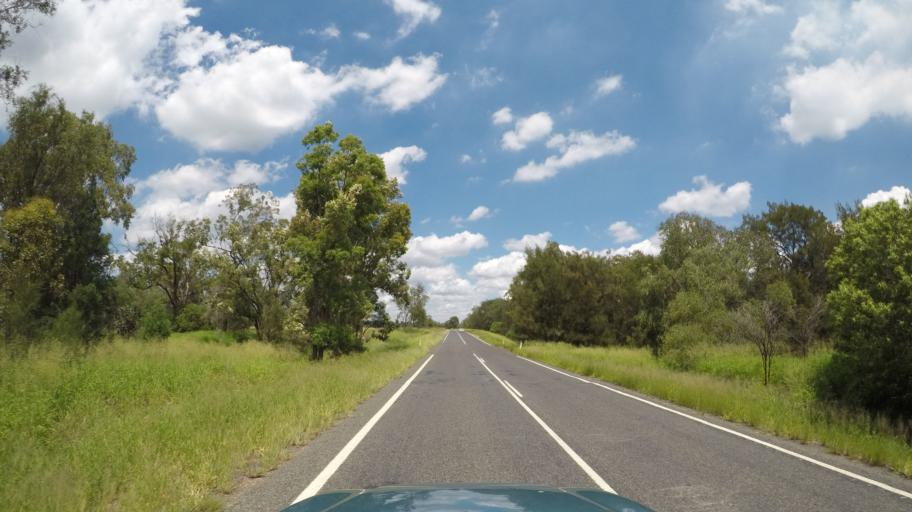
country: AU
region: Queensland
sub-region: Western Downs
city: Dalby
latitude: -27.9529
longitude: 151.1347
